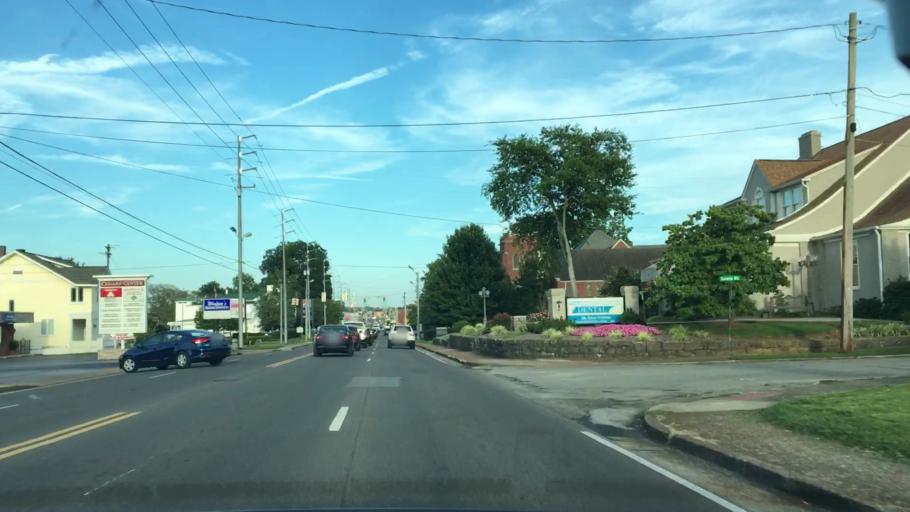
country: US
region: Tennessee
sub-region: Wilson County
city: Lebanon
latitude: 36.2086
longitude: -86.2976
